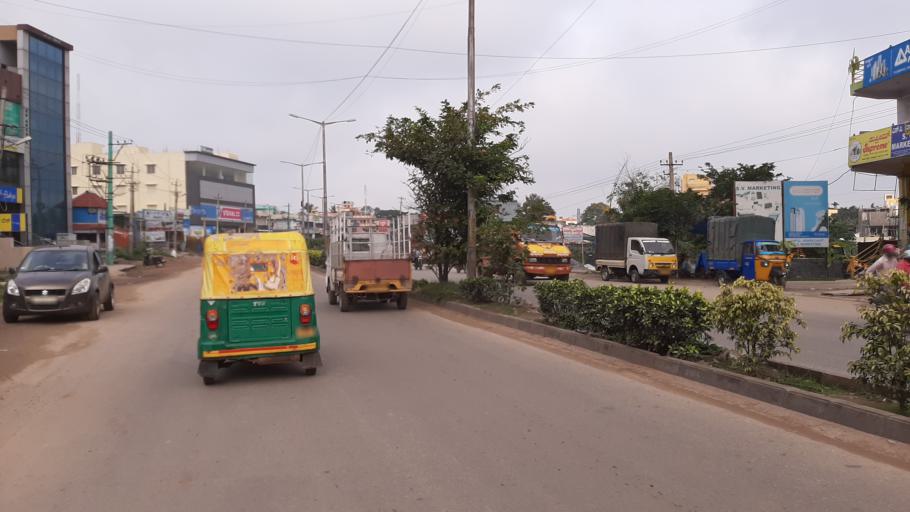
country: IN
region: Karnataka
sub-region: Bangalore Urban
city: Bangalore
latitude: 12.9852
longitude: 77.4849
